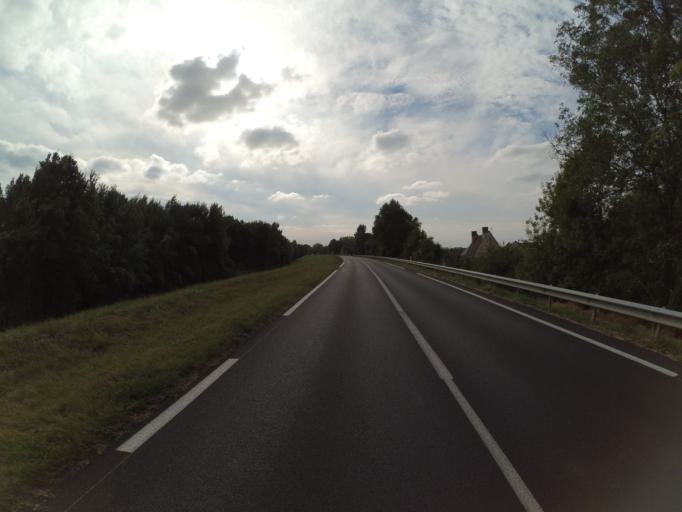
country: FR
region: Centre
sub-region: Departement d'Indre-et-Loire
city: Langeais
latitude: 47.2896
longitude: 0.3290
